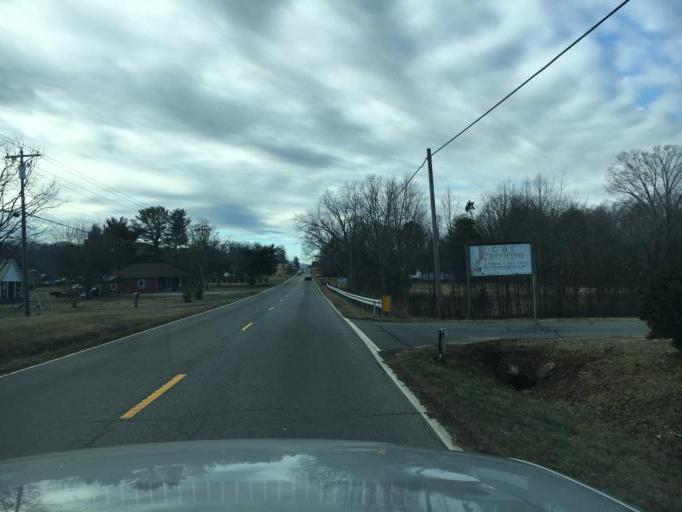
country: US
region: North Carolina
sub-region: Burke County
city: Salem
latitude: 35.6864
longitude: -81.7267
